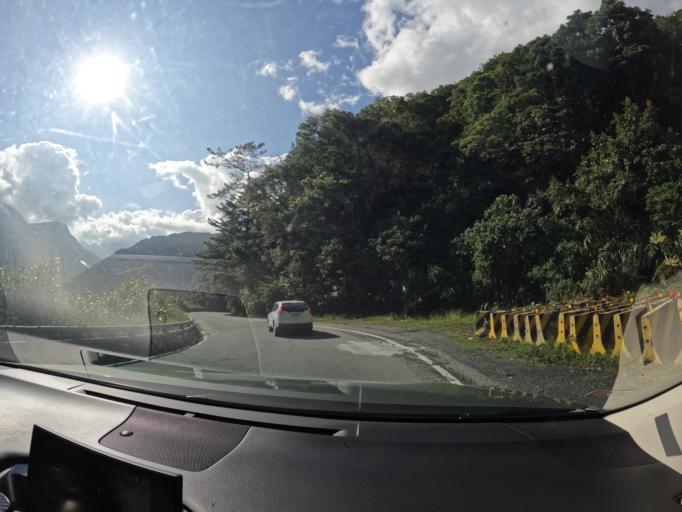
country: TW
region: Taiwan
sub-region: Taitung
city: Taitung
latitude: 23.2001
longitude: 121.0213
